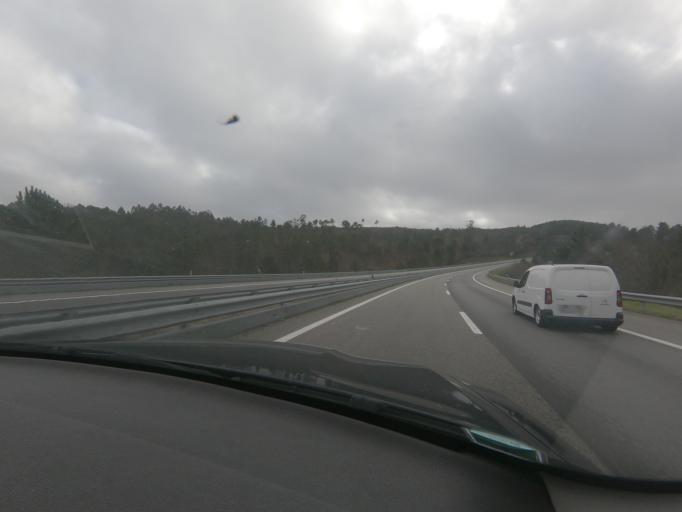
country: PT
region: Viseu
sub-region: Castro Daire
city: Castro Daire
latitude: 40.8430
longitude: -7.9269
